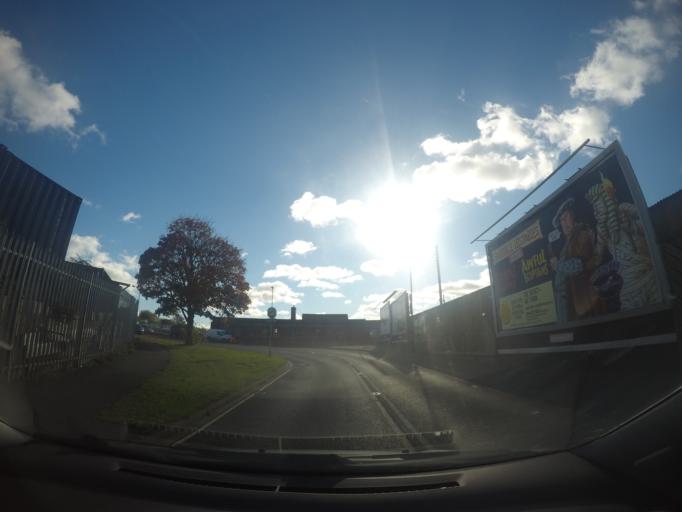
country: GB
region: England
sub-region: City of York
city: York
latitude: 53.9620
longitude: -1.1053
